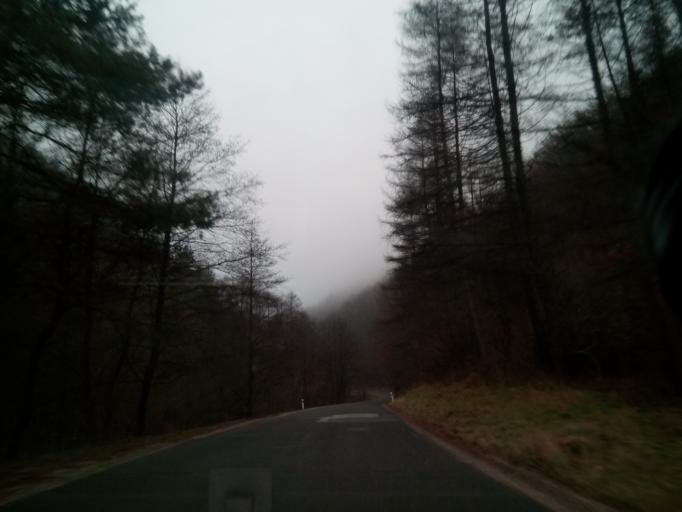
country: SK
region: Kosicky
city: Krompachy
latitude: 48.9461
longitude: 20.9488
